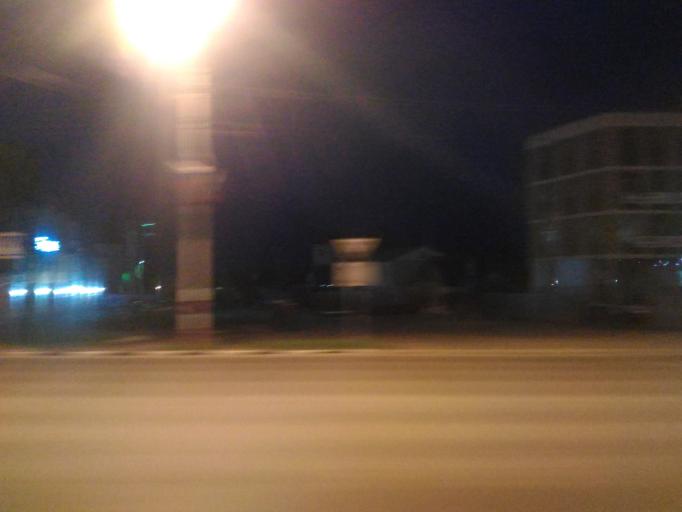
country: RU
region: Ulyanovsk
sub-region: Ulyanovskiy Rayon
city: Ulyanovsk
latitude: 54.2961
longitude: 48.3768
